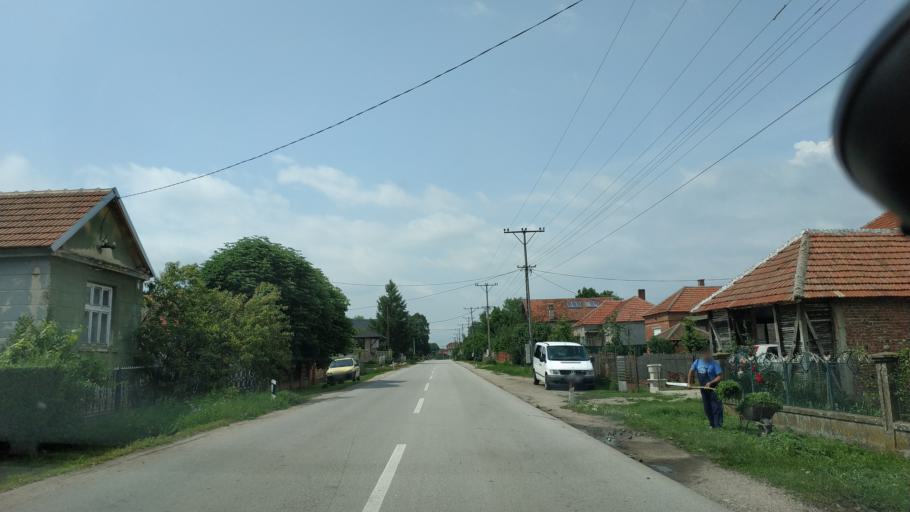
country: RS
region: Central Serbia
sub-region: Nisavski Okrug
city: Aleksinac
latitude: 43.4962
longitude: 21.7066
